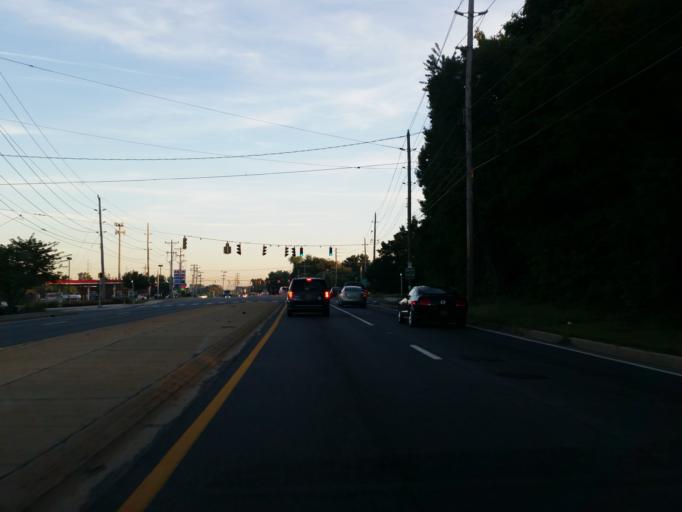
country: US
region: Delaware
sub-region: New Castle County
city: Brookside
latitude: 39.6593
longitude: -75.7353
